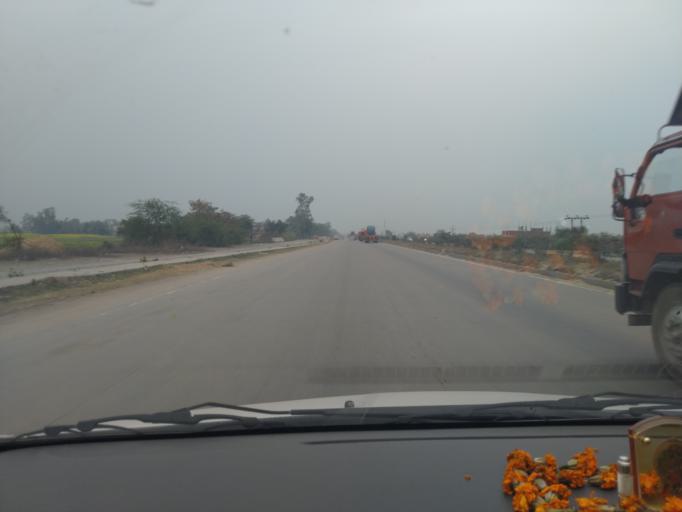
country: IN
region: Bihar
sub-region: Rohtas
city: Dehri
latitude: 24.9698
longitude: 83.9190
